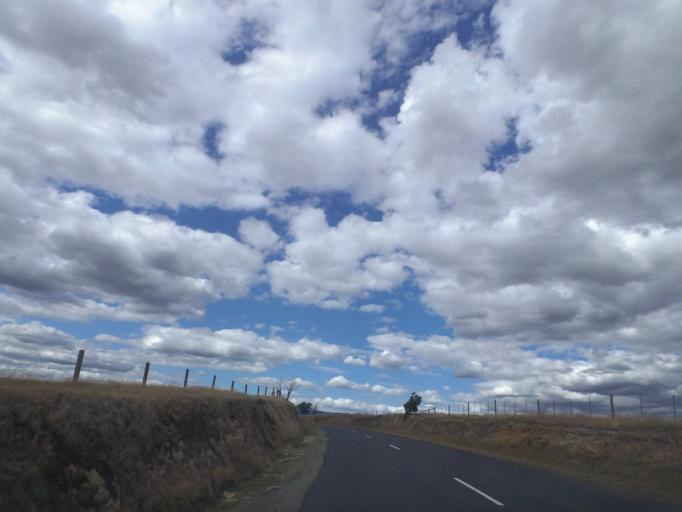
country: AU
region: Victoria
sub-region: Yarra Ranges
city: Yarra Glen
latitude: -37.6437
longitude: 145.4183
